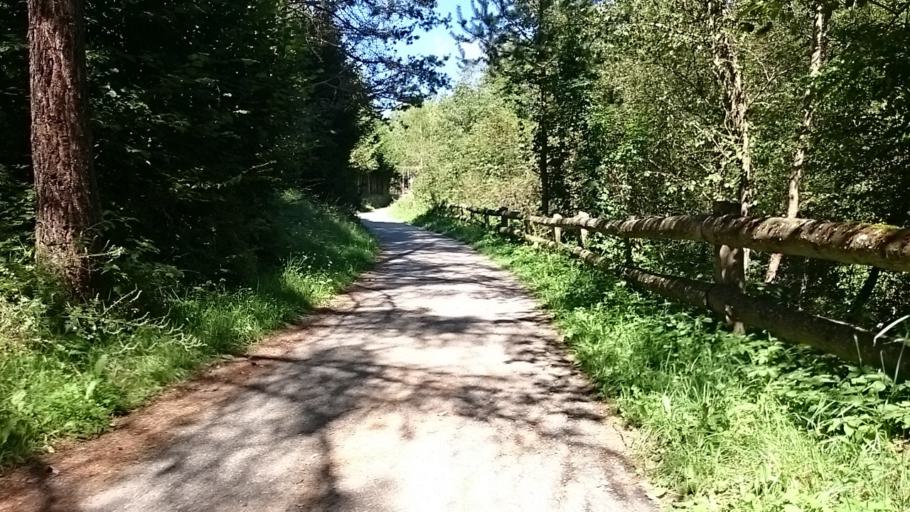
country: IT
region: Trentino-Alto Adige
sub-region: Bolzano
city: Perca
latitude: 46.7863
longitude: 11.9686
